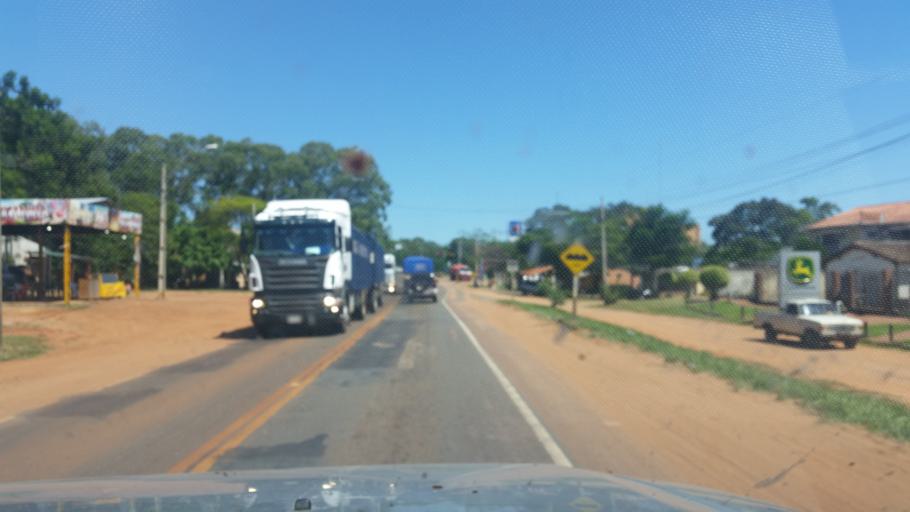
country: PY
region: Misiones
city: San Juan Bautista
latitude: -26.6653
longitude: -57.1326
